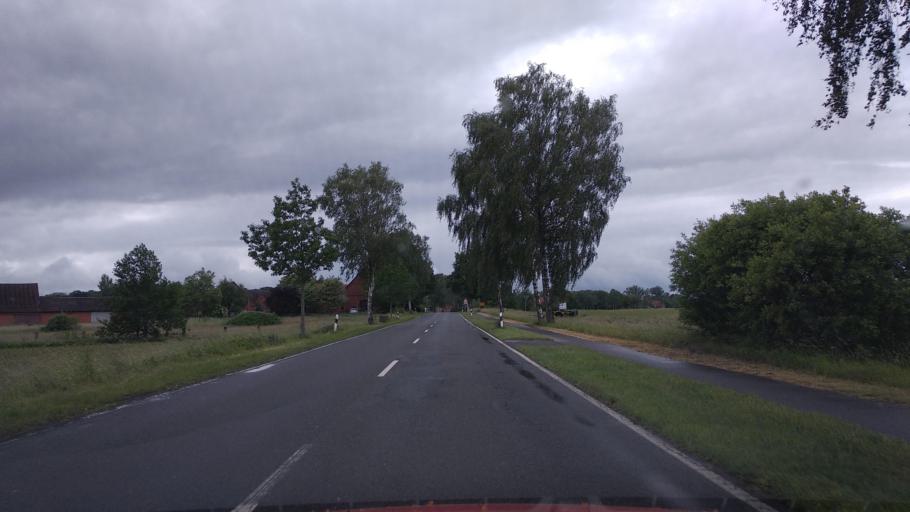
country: DE
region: Lower Saxony
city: Auhagen
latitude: 52.4059
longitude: 9.3152
